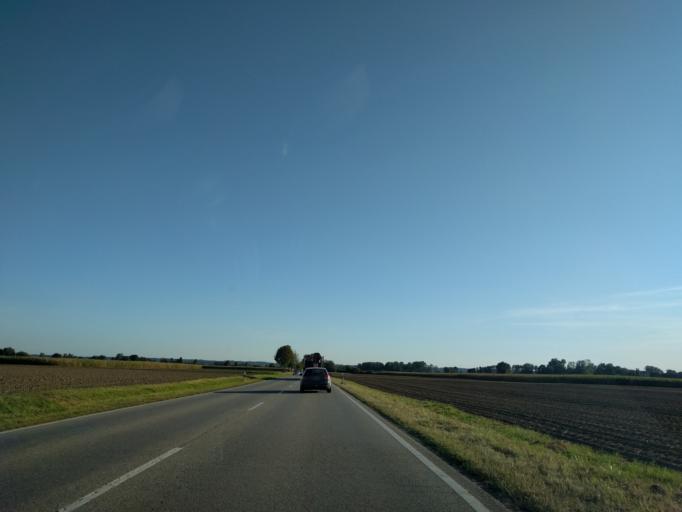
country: DE
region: Bavaria
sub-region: Lower Bavaria
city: Osterhofen
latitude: 48.7083
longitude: 13.0454
